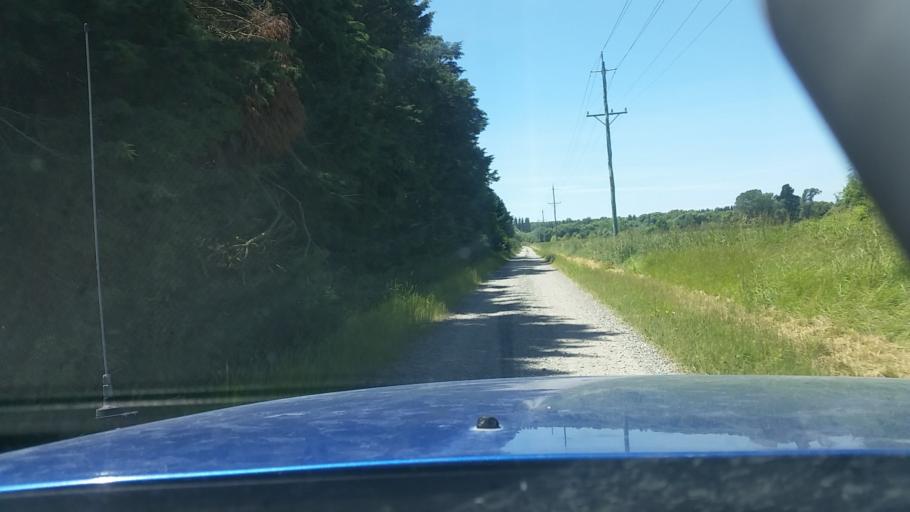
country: NZ
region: Canterbury
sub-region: Ashburton District
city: Tinwald
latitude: -43.9466
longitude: 171.7694
